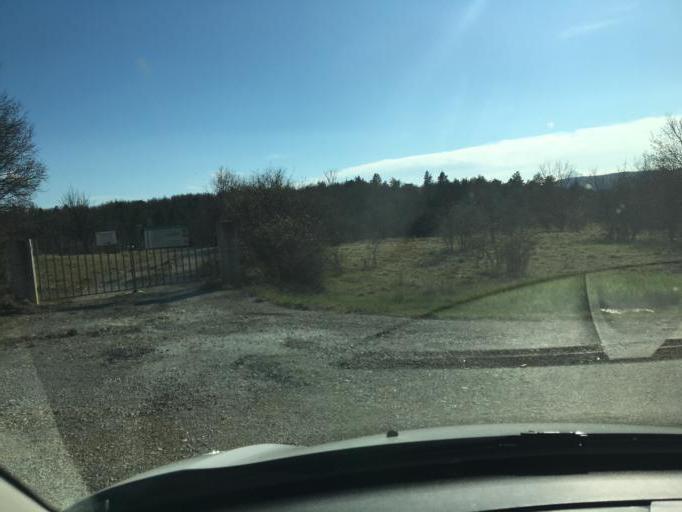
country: FR
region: Provence-Alpes-Cote d'Azur
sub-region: Departement du Vaucluse
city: Sault
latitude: 44.0836
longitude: 5.4093
